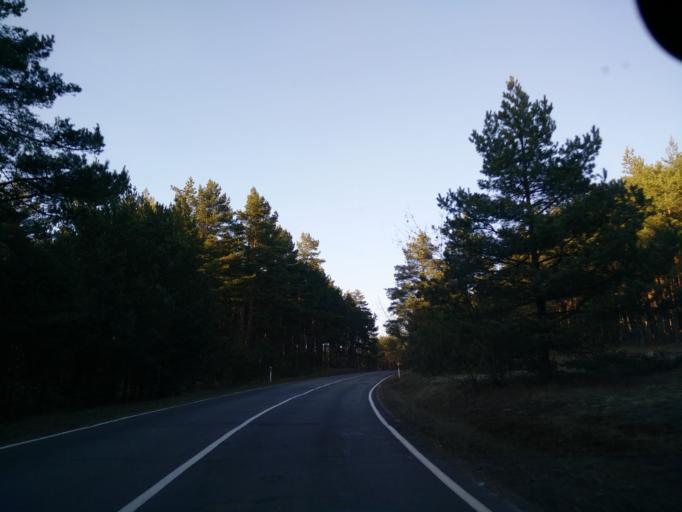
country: LT
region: Klaipedos apskritis
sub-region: Klaipeda
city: Klaipeda
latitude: 55.6622
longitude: 21.1159
